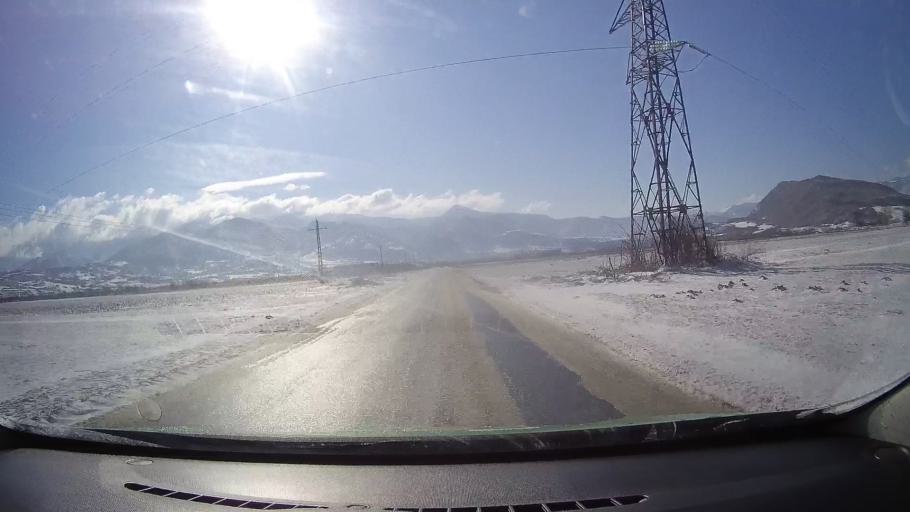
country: RO
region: Sibiu
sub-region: Comuna Turnu Rosu
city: Turnu Rosu
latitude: 45.6597
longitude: 24.2967
